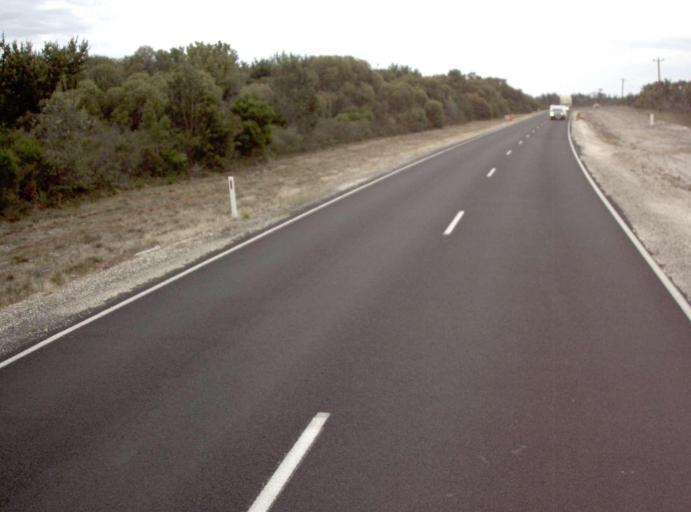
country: AU
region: Victoria
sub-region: East Gippsland
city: Bairnsdale
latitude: -38.0999
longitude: 147.5057
